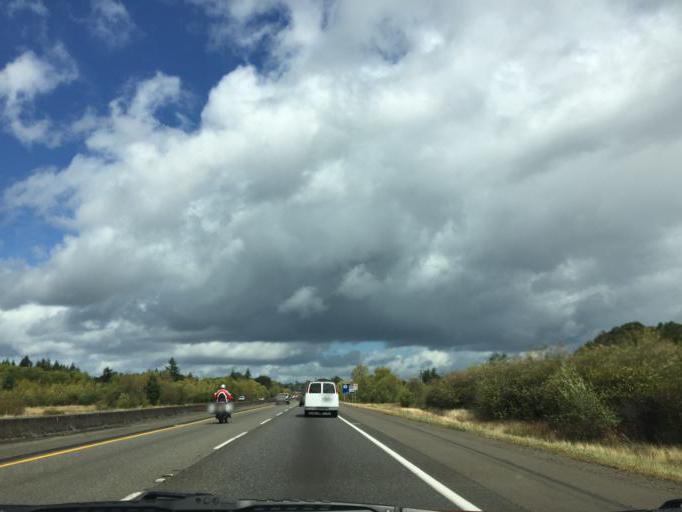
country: US
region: Washington
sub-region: Lewis County
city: Winlock
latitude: 46.4585
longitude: -122.8858
